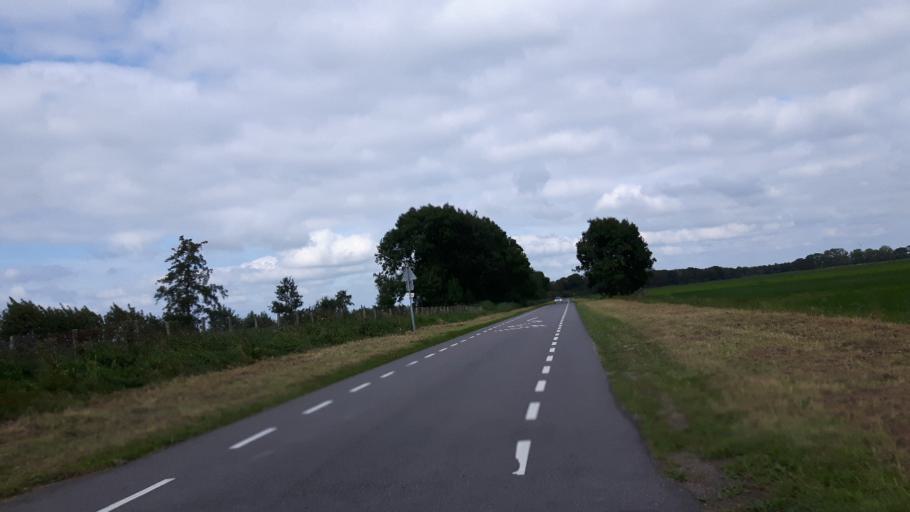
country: NL
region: Utrecht
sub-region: Stichtse Vecht
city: Breukelen
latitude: 52.1755
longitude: 4.9577
